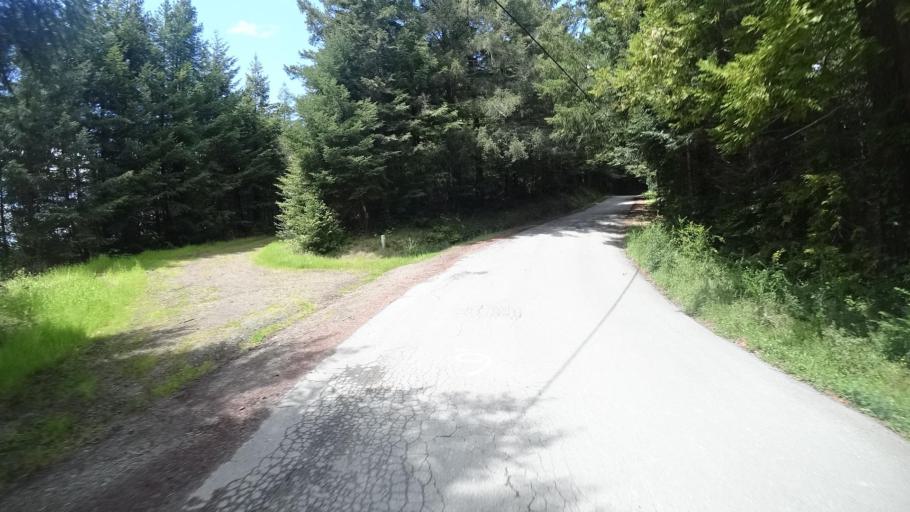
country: US
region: California
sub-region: Humboldt County
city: Blue Lake
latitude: 40.8015
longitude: -123.8796
